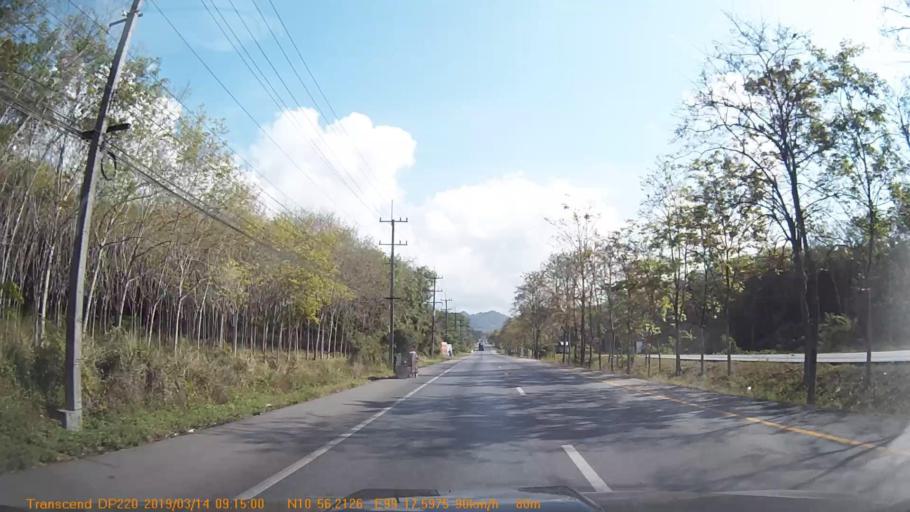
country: TH
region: Prachuap Khiri Khan
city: Bang Saphan Noi
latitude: 10.9377
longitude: 99.2937
